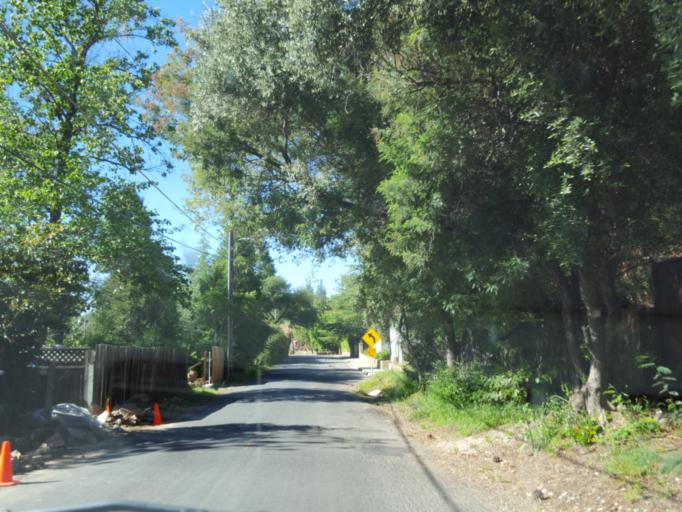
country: US
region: California
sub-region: Placer County
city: Auburn
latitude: 38.8946
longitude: -121.0616
